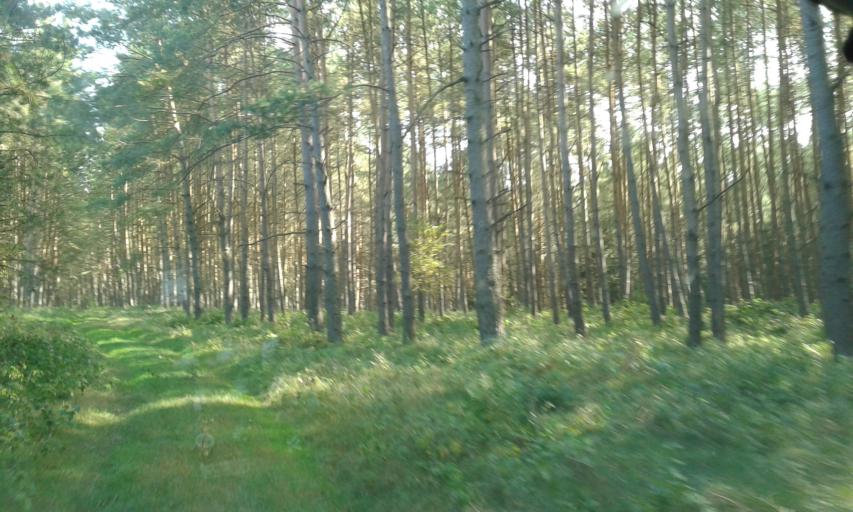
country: PL
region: West Pomeranian Voivodeship
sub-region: Powiat stargardzki
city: Suchan
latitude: 53.2442
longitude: 15.3540
